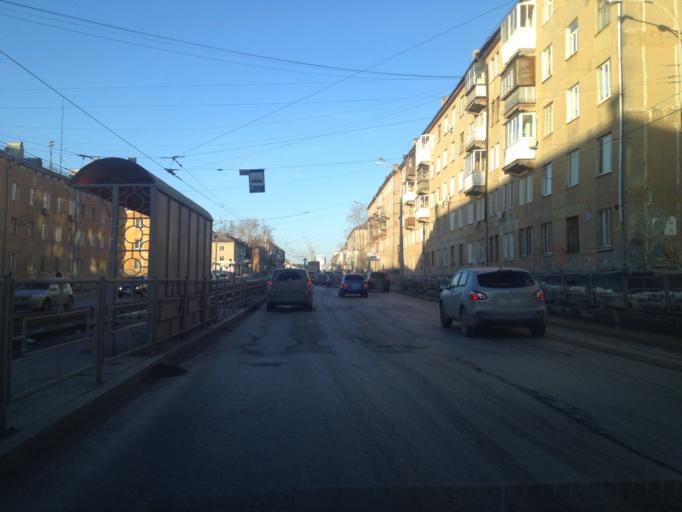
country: RU
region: Sverdlovsk
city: Yekaterinburg
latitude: 56.8840
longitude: 60.5625
